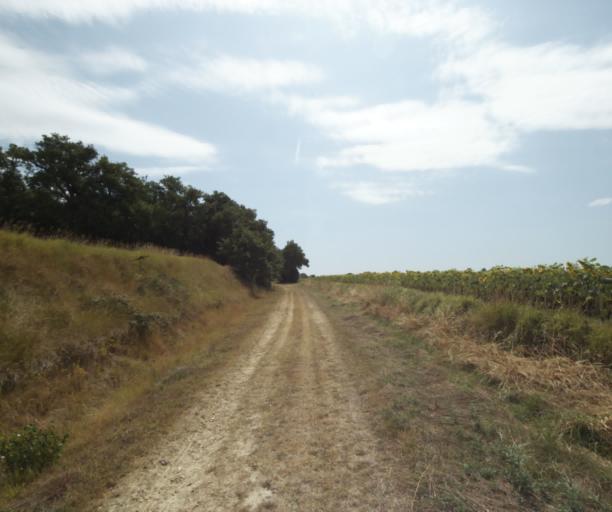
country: FR
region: Midi-Pyrenees
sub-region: Departement de la Haute-Garonne
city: Saint-Felix-Lauragais
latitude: 43.4305
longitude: 1.9161
